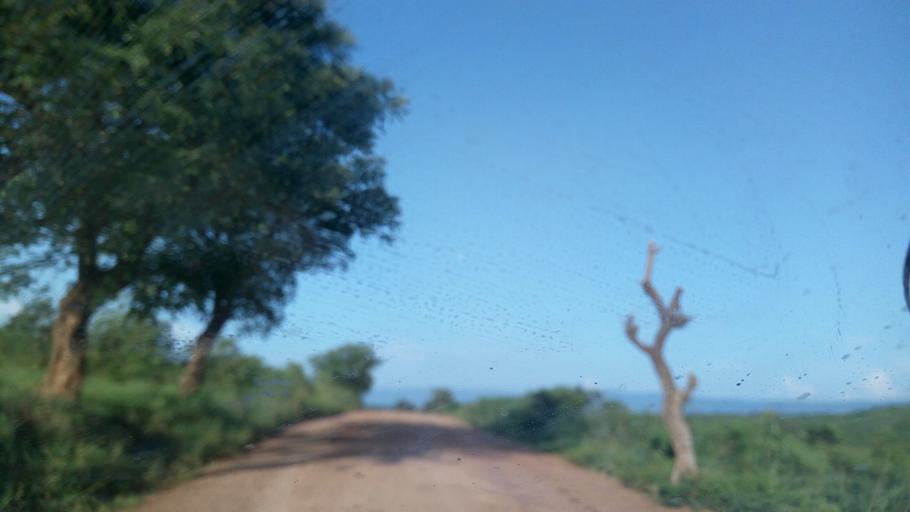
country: BI
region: Bururi
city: Rumonge
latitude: -4.2004
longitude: 29.0242
